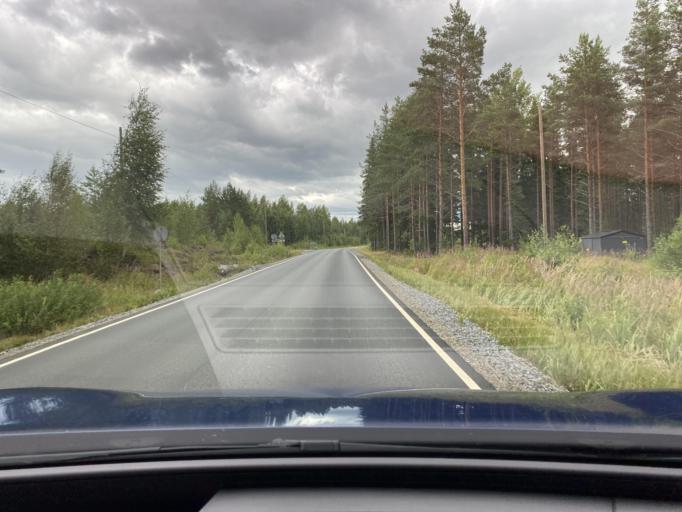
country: FI
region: Pirkanmaa
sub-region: Lounais-Pirkanmaa
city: Punkalaidun
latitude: 61.2713
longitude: 23.0695
